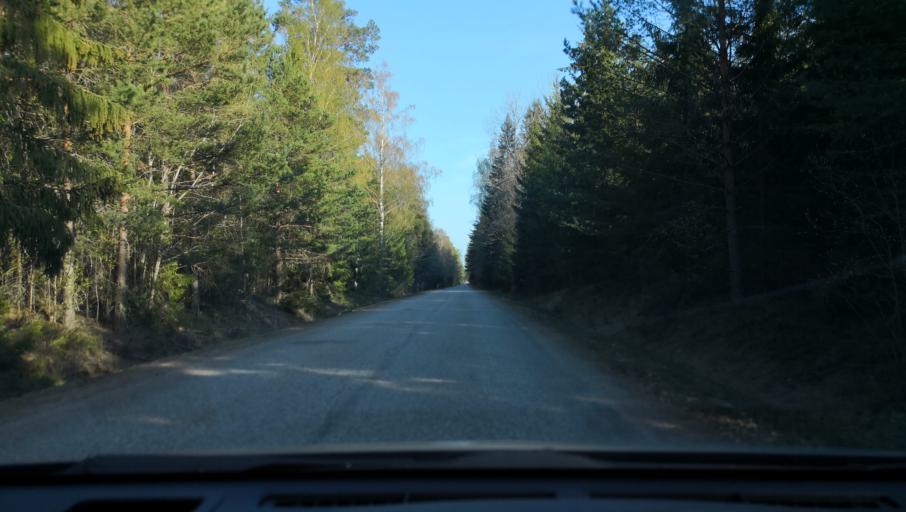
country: SE
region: Uppsala
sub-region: Heby Kommun
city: Tarnsjo
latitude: 60.2749
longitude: 16.8991
